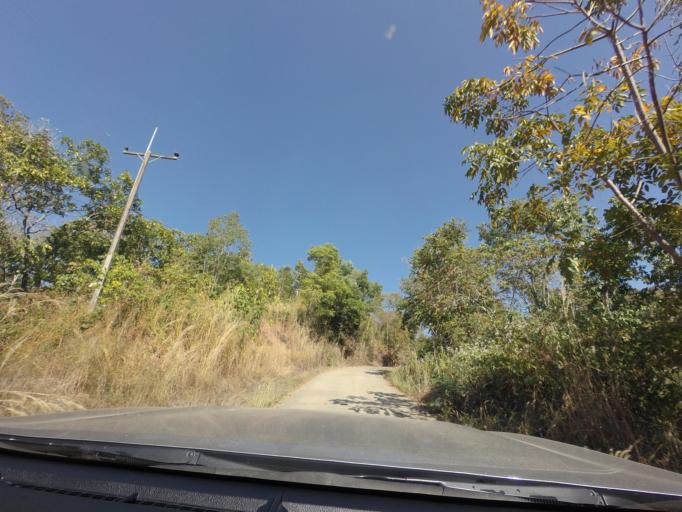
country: TH
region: Lampang
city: Chae Hom
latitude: 18.6156
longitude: 99.6448
